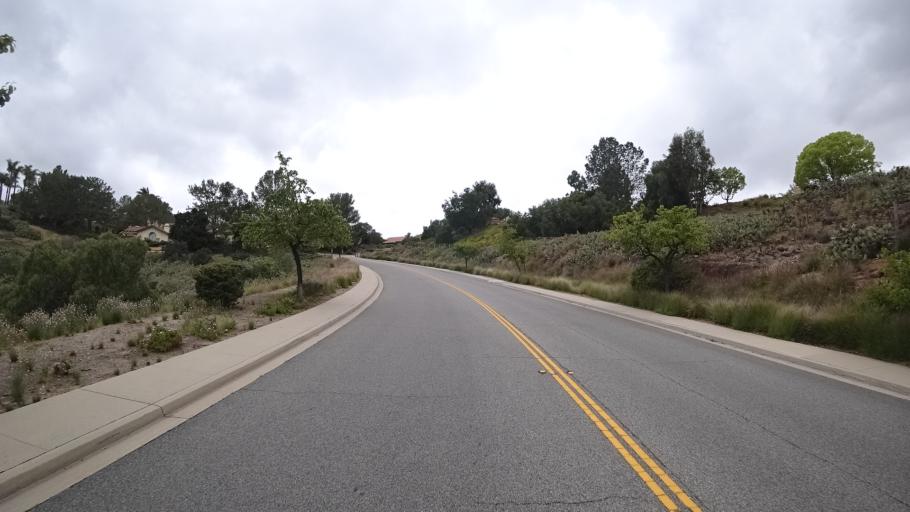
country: US
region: California
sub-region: Ventura County
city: Moorpark
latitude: 34.2281
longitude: -118.8941
